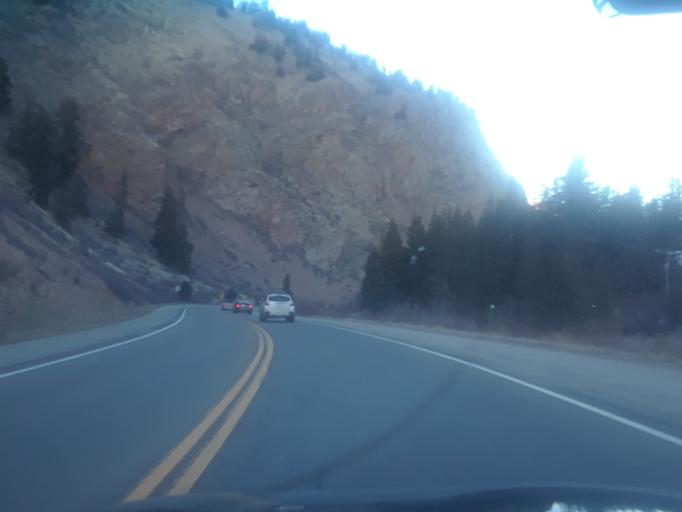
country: US
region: Colorado
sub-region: Clear Creek County
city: Georgetown
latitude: 39.4581
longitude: -105.7095
